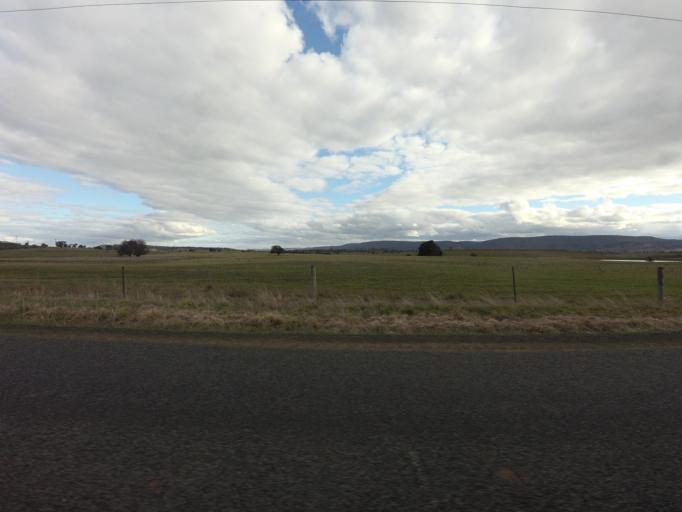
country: AU
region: Tasmania
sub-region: Northern Midlands
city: Evandale
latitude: -41.9202
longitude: 147.4805
